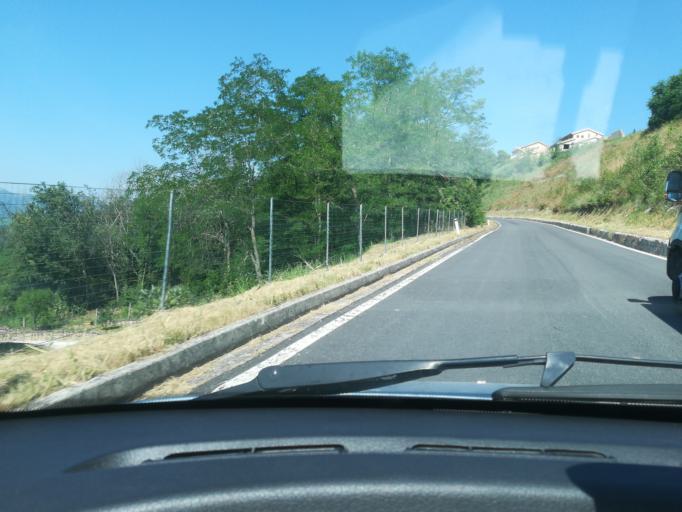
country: IT
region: The Marches
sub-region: Provincia di Macerata
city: San Ginesio
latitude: 43.1063
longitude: 13.3337
